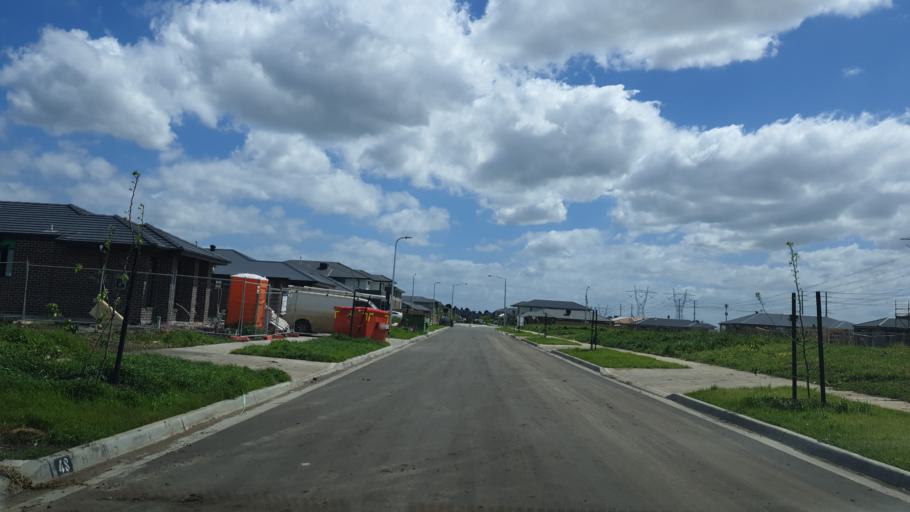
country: AU
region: Victoria
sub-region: Casey
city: Cranbourne
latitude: -38.0934
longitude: 145.3014
